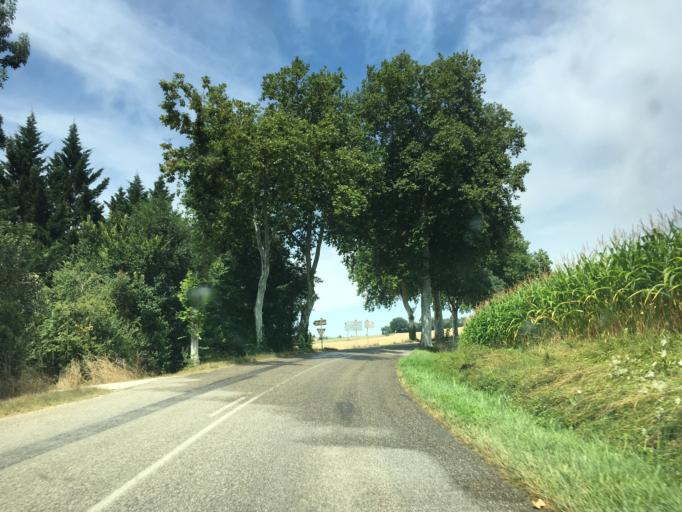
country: FR
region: Midi-Pyrenees
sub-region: Departement du Gers
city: Fleurance
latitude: 43.8540
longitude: 0.6773
